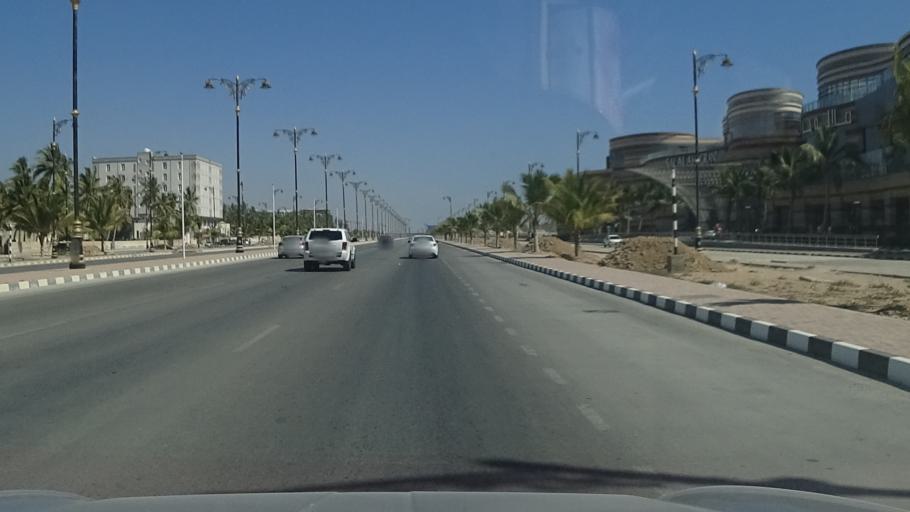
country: OM
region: Zufar
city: Salalah
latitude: 17.0360
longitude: 54.1630
